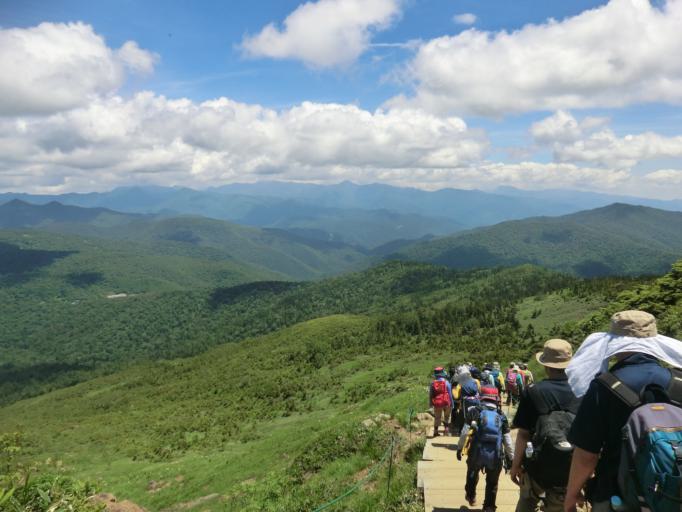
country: JP
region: Gunma
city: Numata
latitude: 36.8945
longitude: 139.1722
